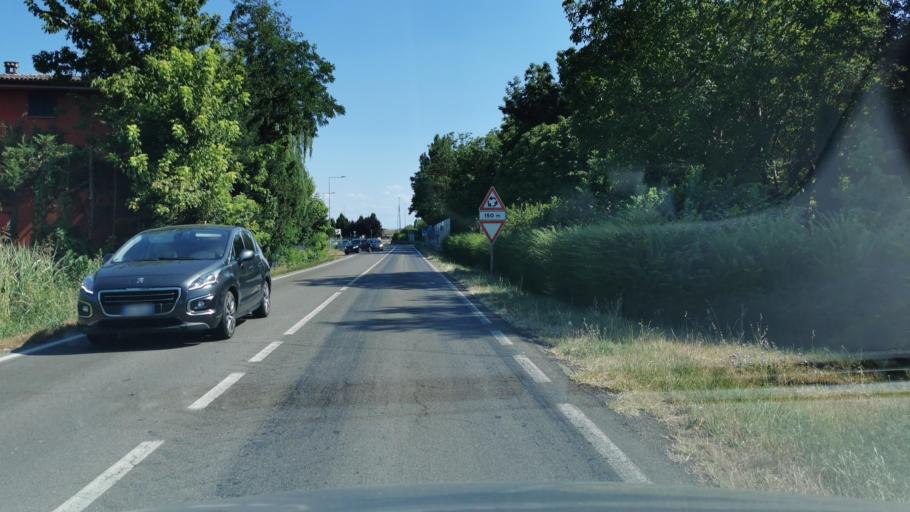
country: IT
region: Emilia-Romagna
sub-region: Provincia di Modena
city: Villanova
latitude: 44.6799
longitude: 10.8940
